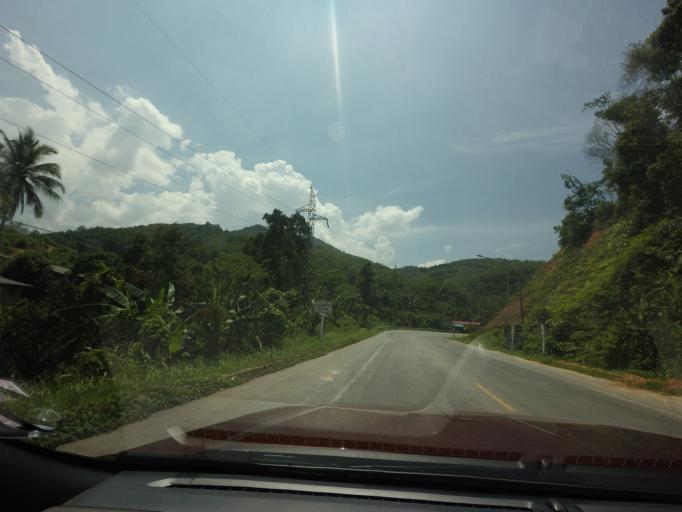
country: TH
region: Yala
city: Betong
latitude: 5.9209
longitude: 101.1629
